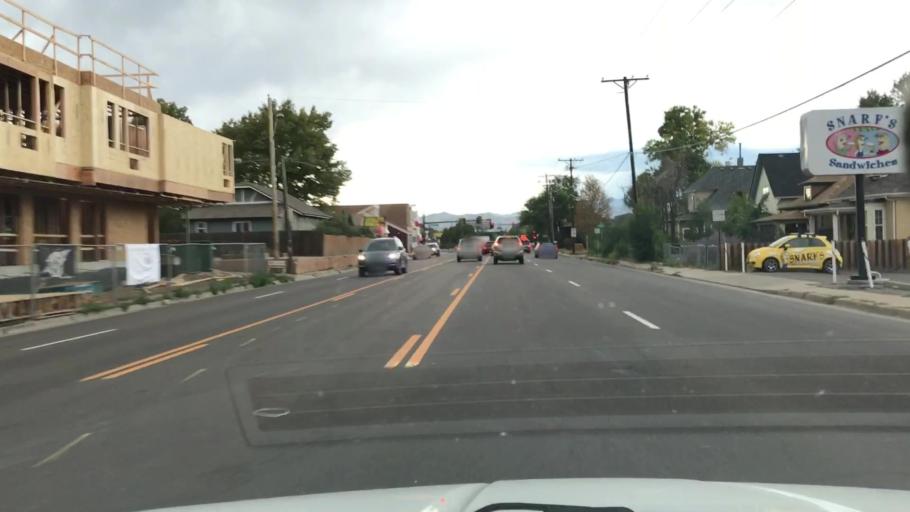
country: US
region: Colorado
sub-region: Jefferson County
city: Edgewater
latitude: 39.7694
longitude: -105.0510
